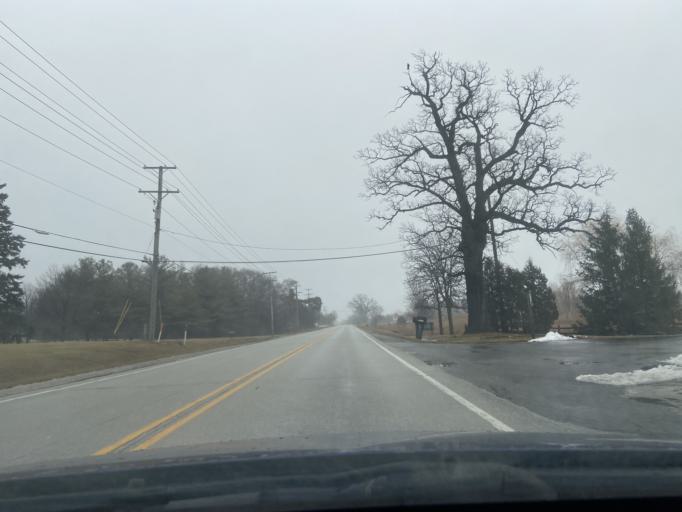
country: US
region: Illinois
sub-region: Lake County
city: Volo
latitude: 42.3203
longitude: -88.1387
